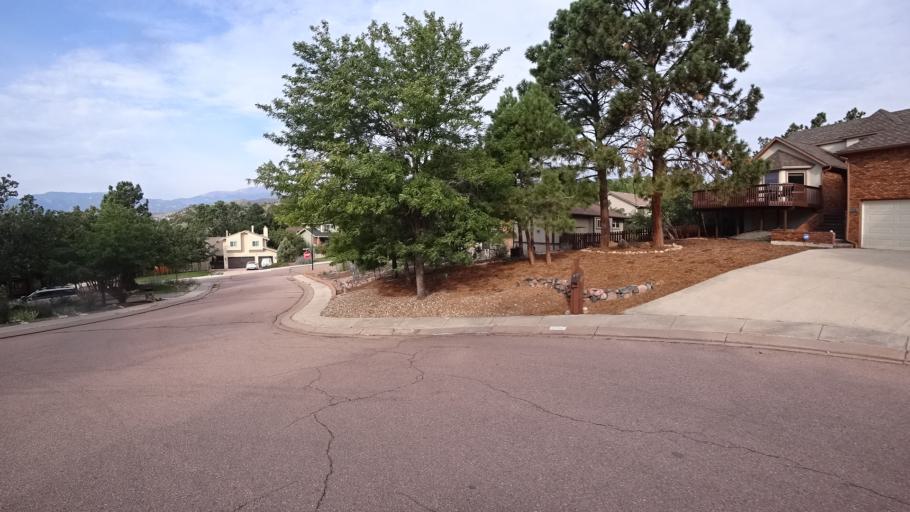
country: US
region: Colorado
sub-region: El Paso County
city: Air Force Academy
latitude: 38.9333
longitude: -104.8439
